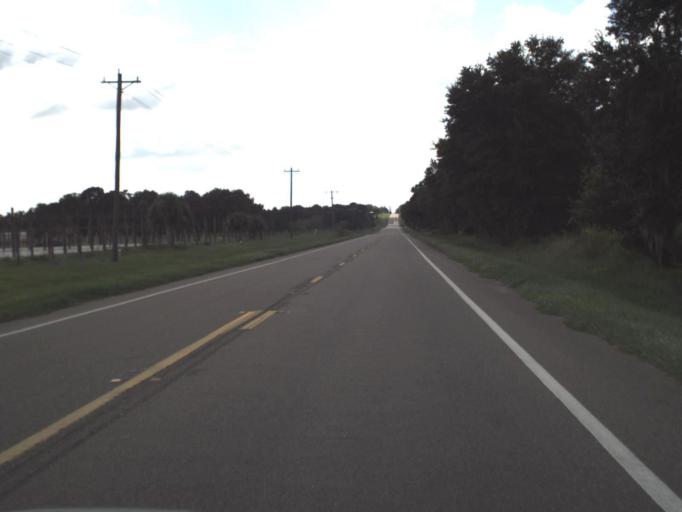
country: US
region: Florida
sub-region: Hardee County
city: Zolfo Springs
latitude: 27.4822
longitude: -81.8569
